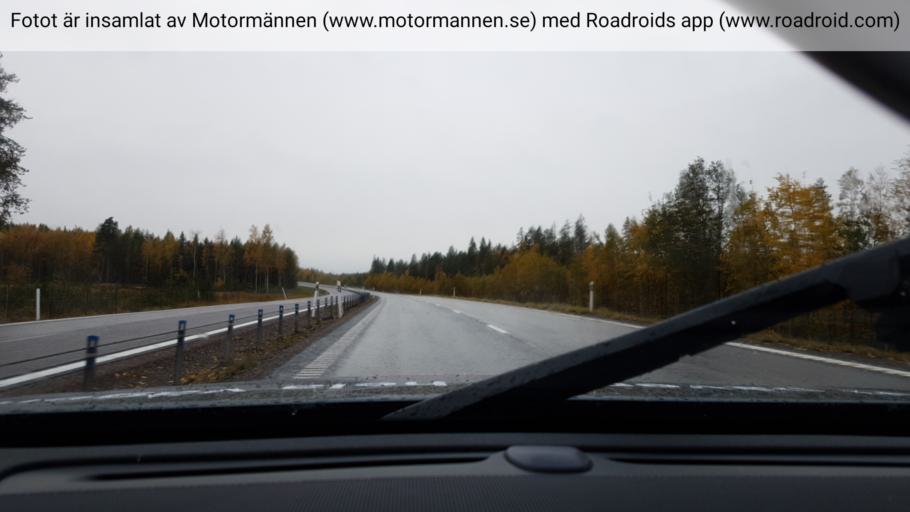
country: SE
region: Norrbotten
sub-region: Lulea Kommun
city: Gammelstad
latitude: 65.5821
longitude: 21.9611
